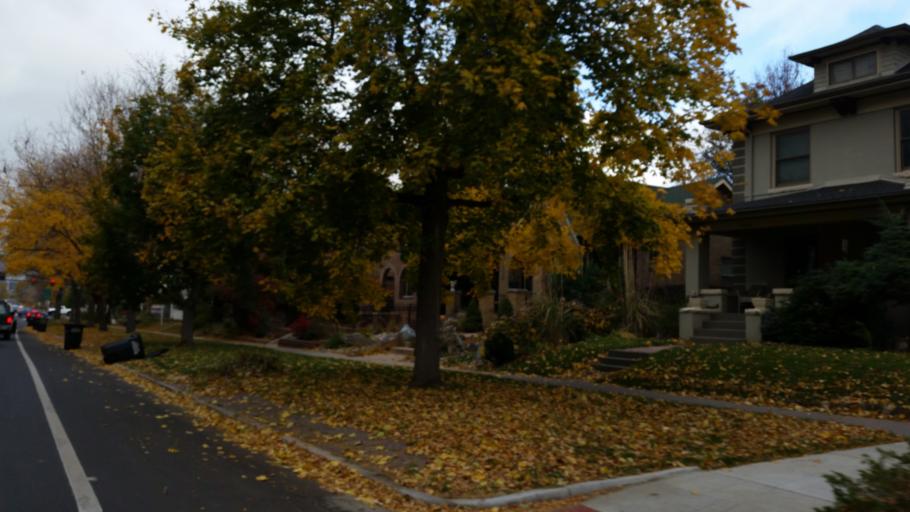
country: US
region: Colorado
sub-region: Arapahoe County
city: Glendale
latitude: 39.7438
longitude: -104.9391
